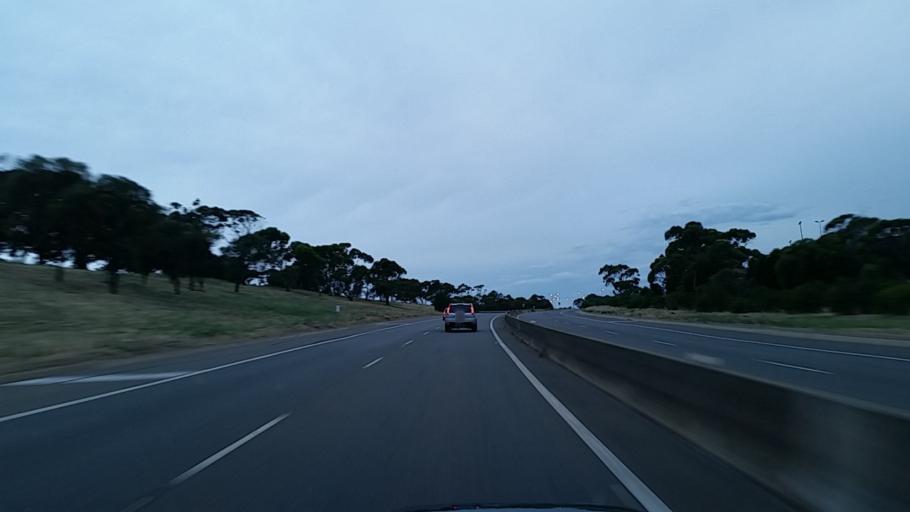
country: AU
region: South Australia
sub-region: Onkaparinga
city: Reynella
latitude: -35.0864
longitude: 138.5015
